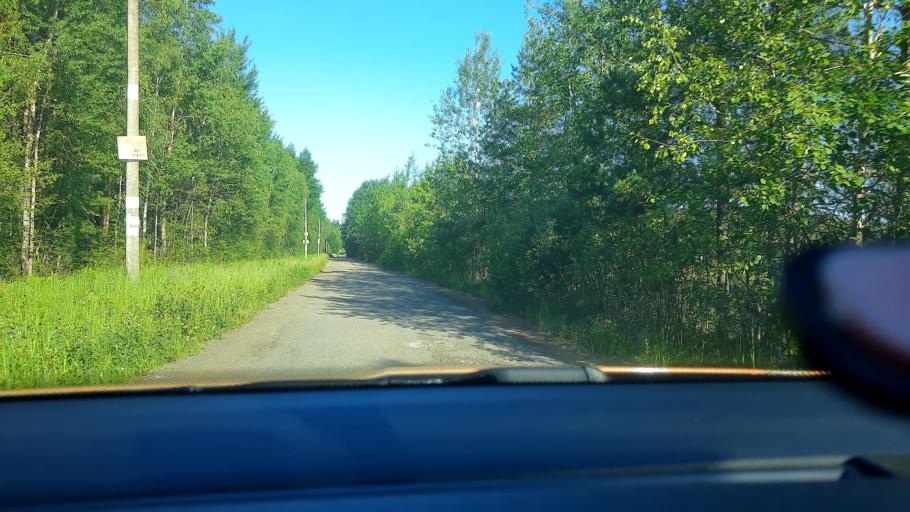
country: RU
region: Moskovskaya
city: Elektrogorsk
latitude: 55.8985
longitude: 38.7085
